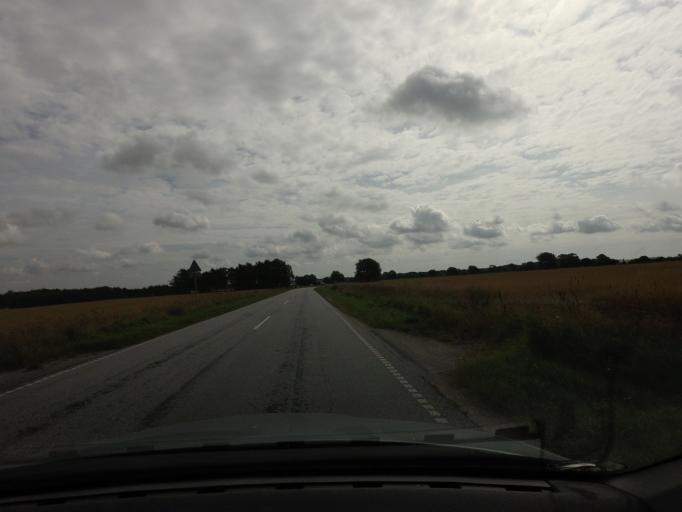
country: DK
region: North Denmark
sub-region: Bronderslev Kommune
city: Dronninglund
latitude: 57.2837
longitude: 10.2411
